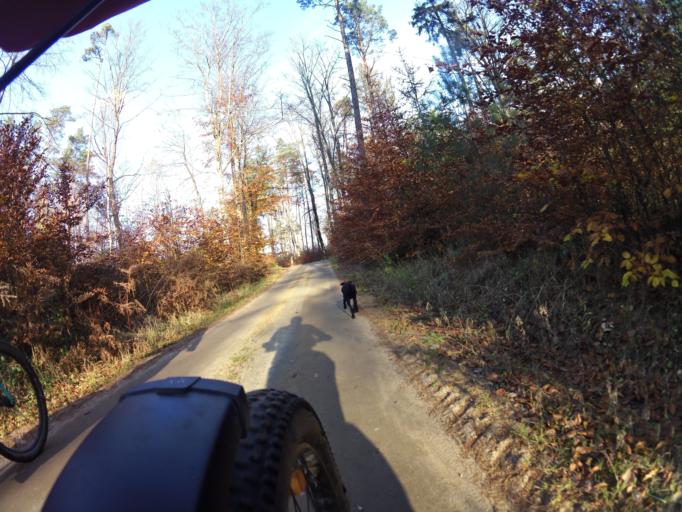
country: PL
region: Pomeranian Voivodeship
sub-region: Powiat pucki
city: Krokowa
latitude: 54.7253
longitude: 18.2155
